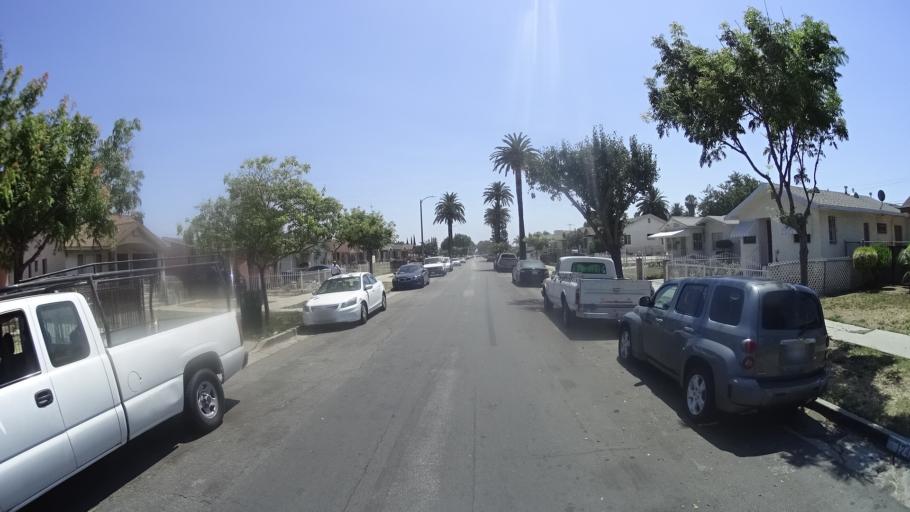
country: US
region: California
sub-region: Los Angeles County
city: Westmont
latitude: 33.9727
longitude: -118.2978
